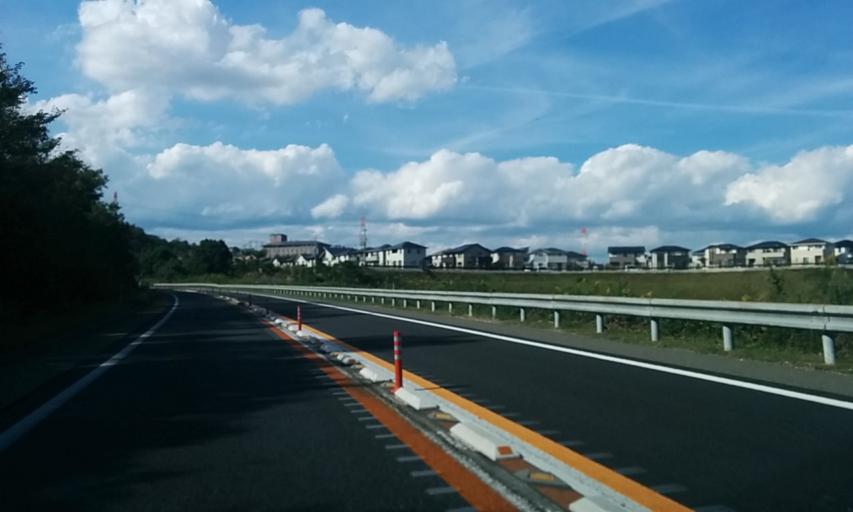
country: JP
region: Kyoto
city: Tanabe
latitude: 34.7846
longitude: 135.7712
